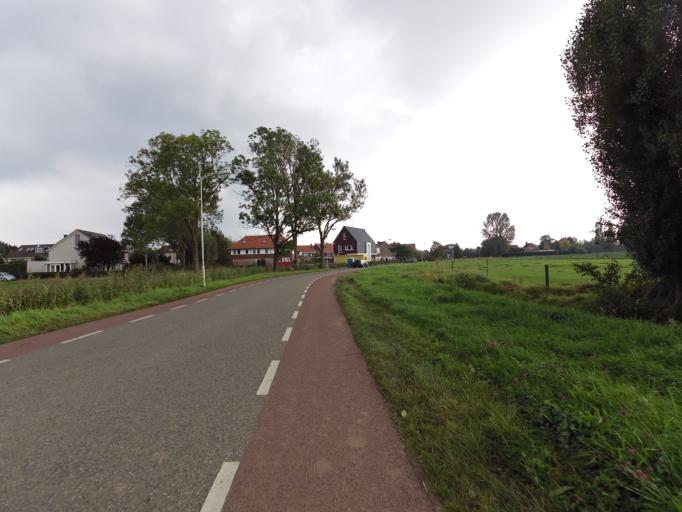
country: NL
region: Gelderland
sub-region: Gemeente Duiven
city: Duiven
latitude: 51.9426
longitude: 5.9965
